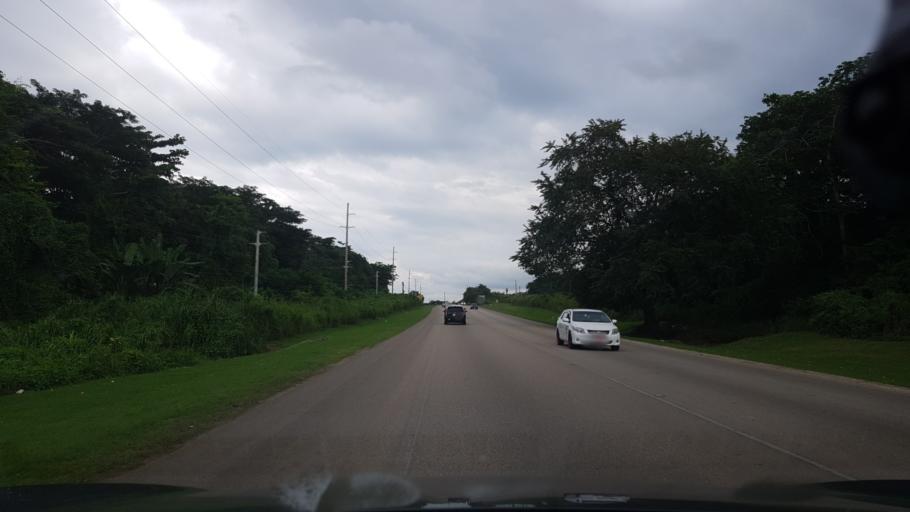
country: JM
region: Saint Ann
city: Saint Ann's Bay
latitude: 18.4420
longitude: -77.2156
